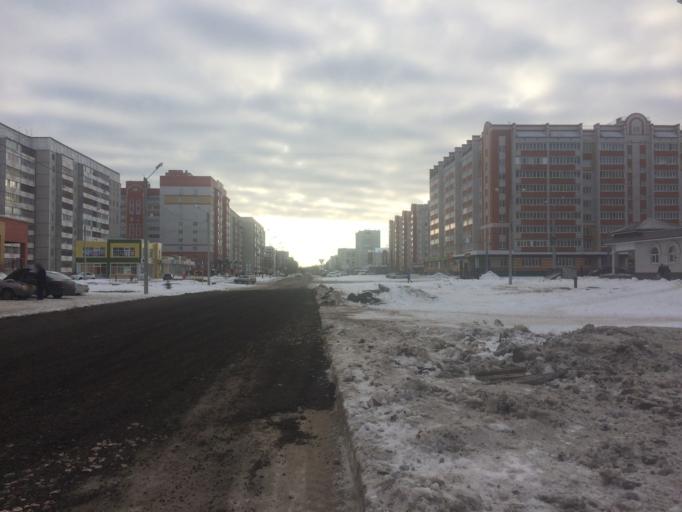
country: RU
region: Mariy-El
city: Yoshkar-Ola
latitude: 56.6404
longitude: 47.9245
